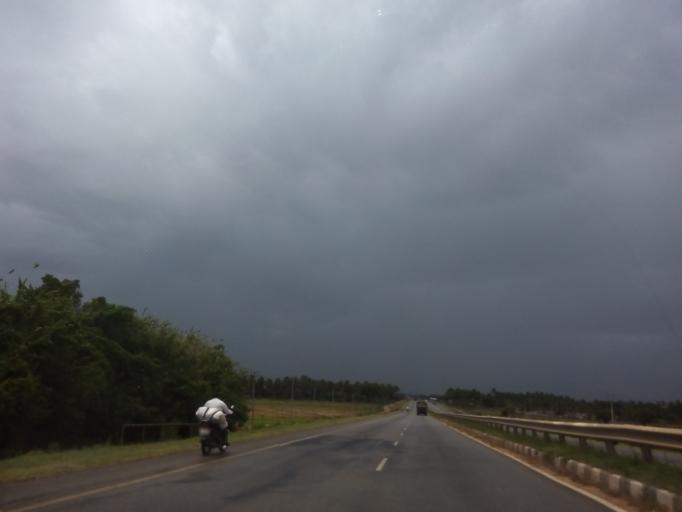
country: IN
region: Karnataka
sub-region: Davanagere
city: Harihar
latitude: 14.4536
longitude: 75.8712
